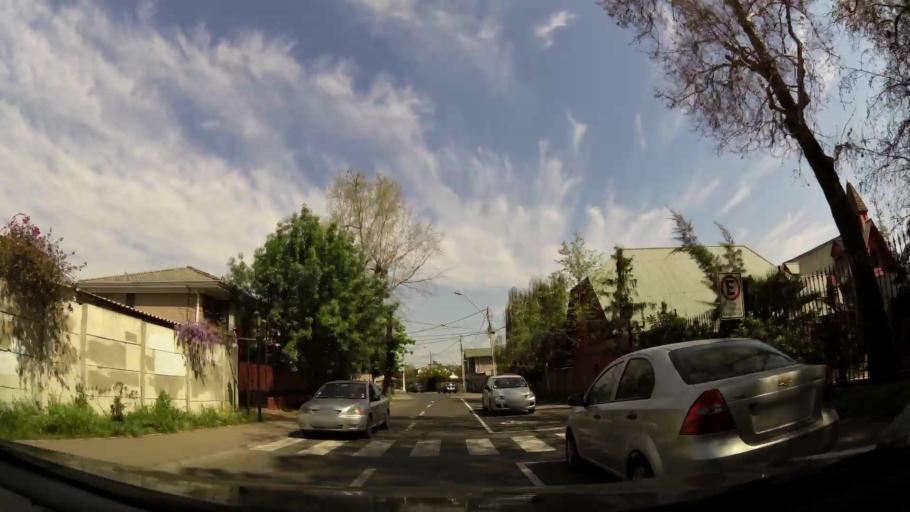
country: CL
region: Santiago Metropolitan
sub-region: Provincia de Cordillera
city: Puente Alto
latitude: -33.5810
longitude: -70.5830
